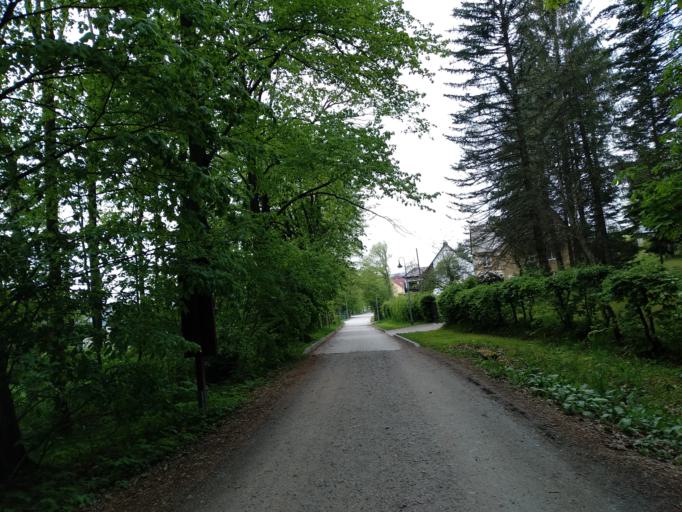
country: DE
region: Saxony
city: Hohnstein
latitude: 50.9739
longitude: 14.1163
